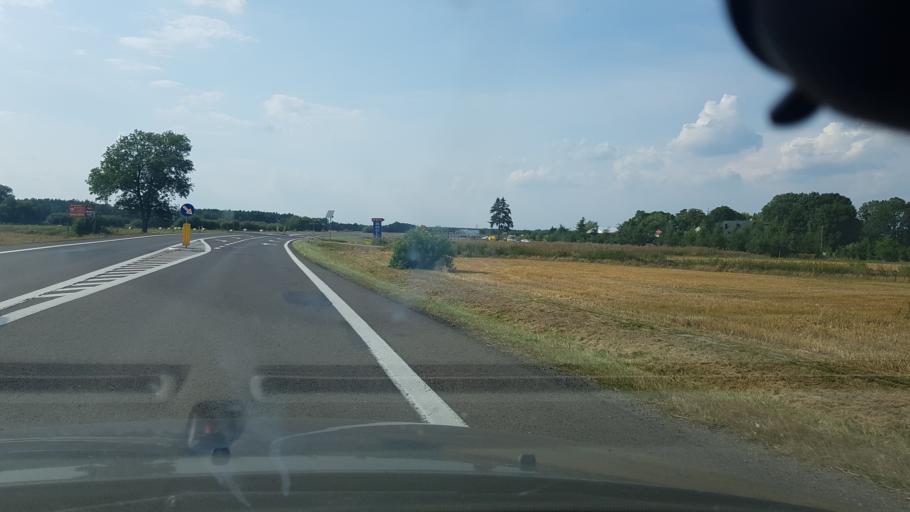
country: PL
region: Masovian Voivodeship
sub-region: Powiat ciechanowski
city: Glinojeck
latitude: 52.7913
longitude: 20.2748
